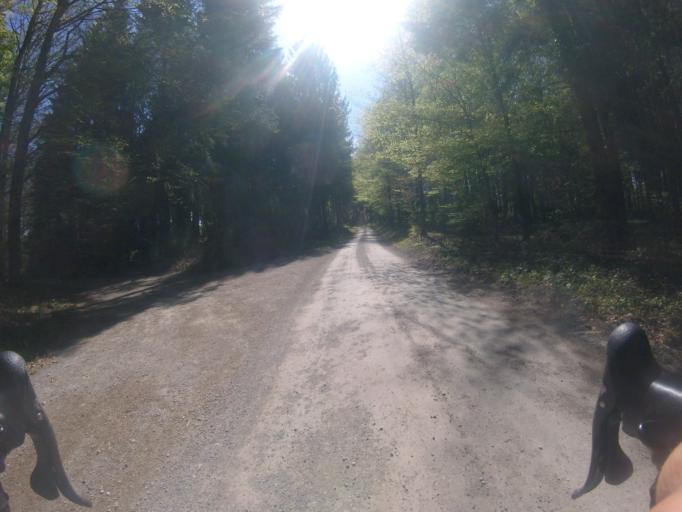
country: CH
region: Fribourg
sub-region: Sense District
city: Flamatt
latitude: 46.9142
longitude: 7.2961
